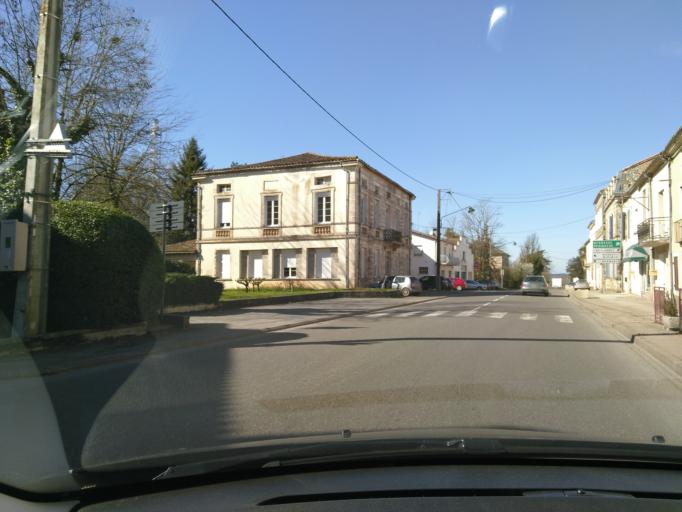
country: FR
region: Aquitaine
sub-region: Departement du Lot-et-Garonne
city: Cancon
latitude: 44.5362
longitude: 0.6237
